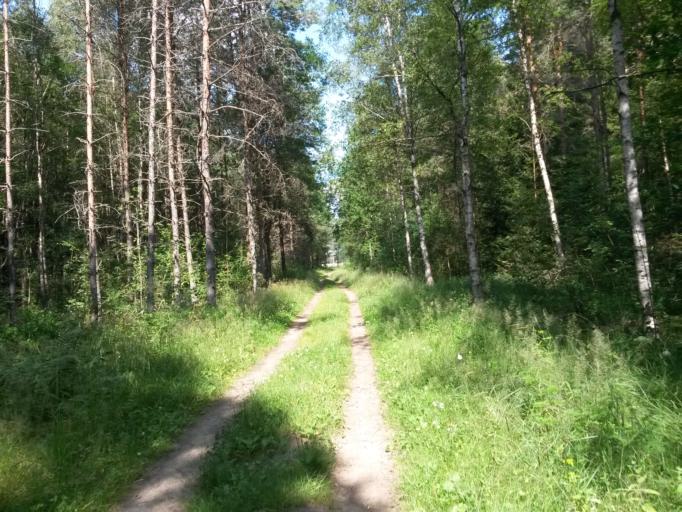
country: SE
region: Vaestra Goetaland
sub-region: Vargarda Kommun
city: Vargarda
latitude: 58.0390
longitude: 12.8313
